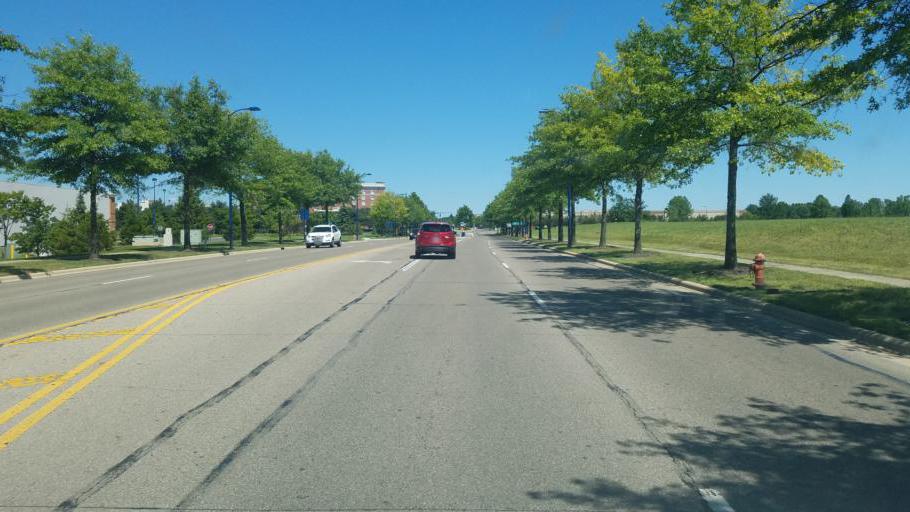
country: US
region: Ohio
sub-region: Franklin County
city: Minerva Park
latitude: 40.0490
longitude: -82.9233
